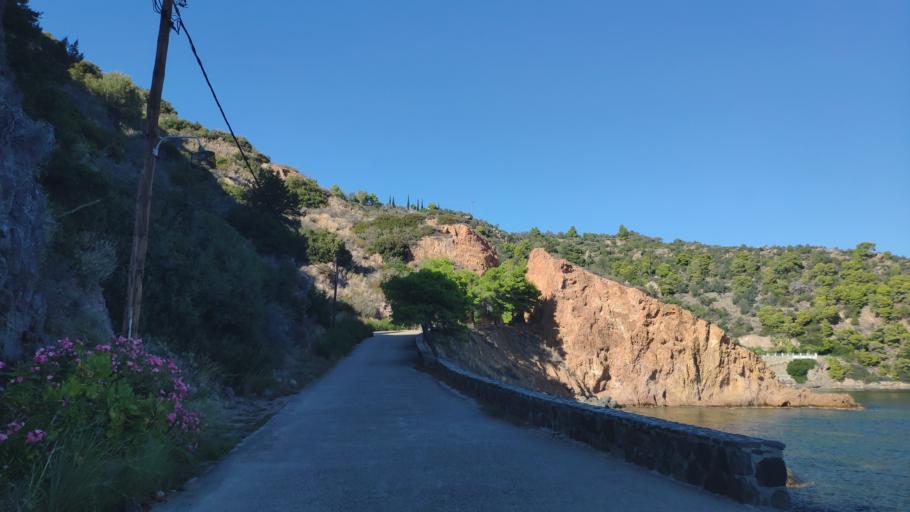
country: GR
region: Attica
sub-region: Nomos Piraios
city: Poros
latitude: 37.5883
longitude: 23.4020
